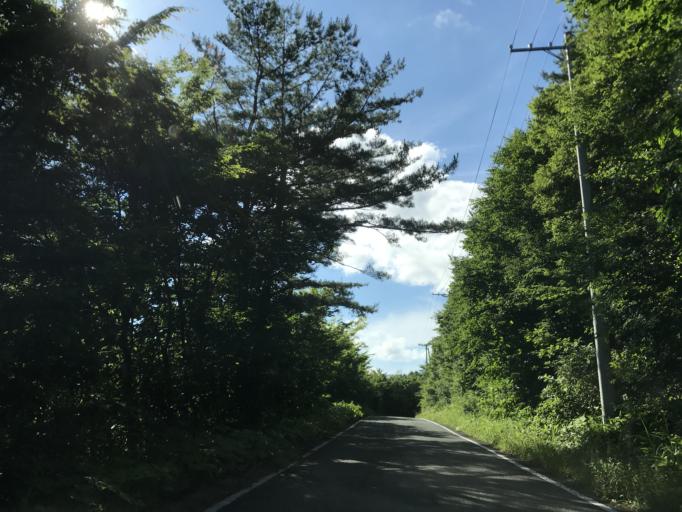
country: JP
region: Iwate
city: Ichinoseki
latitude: 38.8998
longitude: 140.8807
